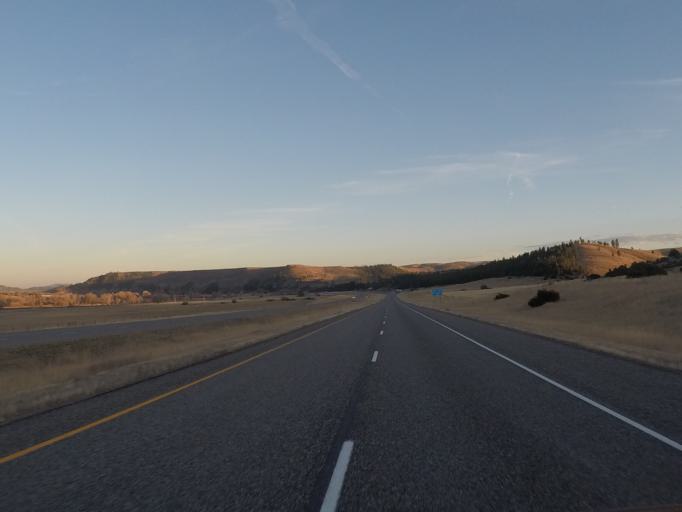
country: US
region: Montana
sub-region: Sweet Grass County
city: Big Timber
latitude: 45.7424
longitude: -109.7676
